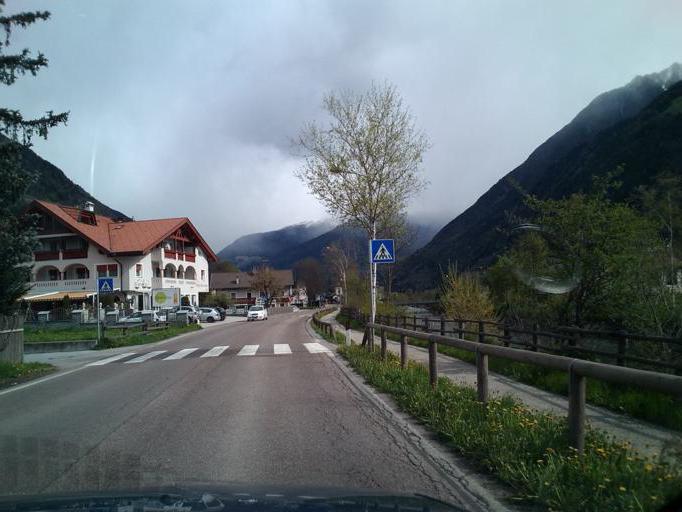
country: IT
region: Trentino-Alto Adige
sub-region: Bolzano
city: Gais
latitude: 46.8638
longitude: 11.9484
